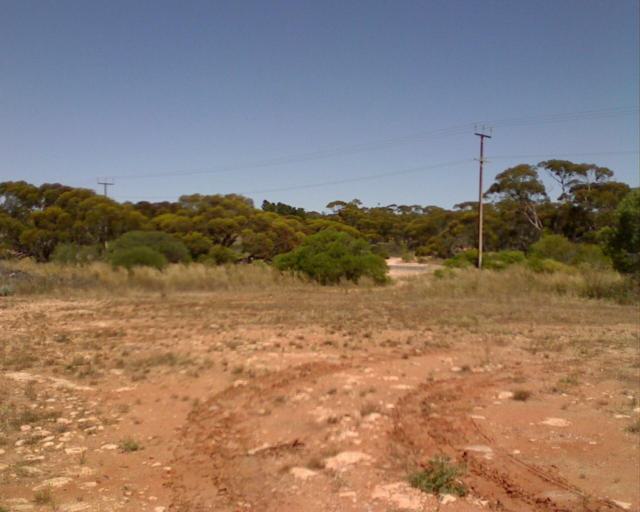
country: AU
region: South Australia
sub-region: Kimba
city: Caralue
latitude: -33.1334
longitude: 135.5520
